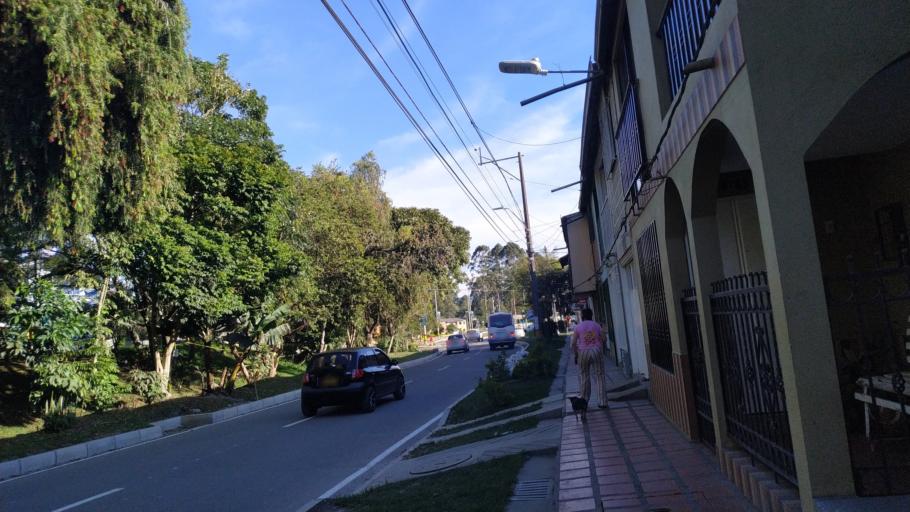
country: CO
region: Antioquia
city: Rionegro
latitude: 6.1481
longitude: -75.3912
